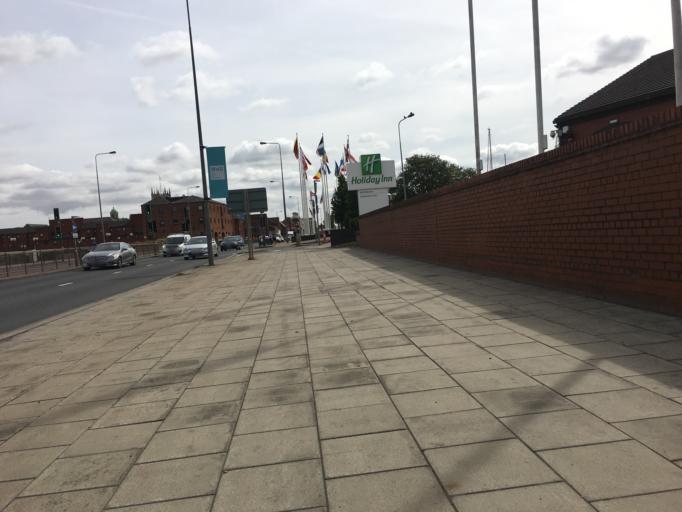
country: GB
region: England
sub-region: City of Kingston upon Hull
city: Hull
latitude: 53.7408
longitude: -0.3406
